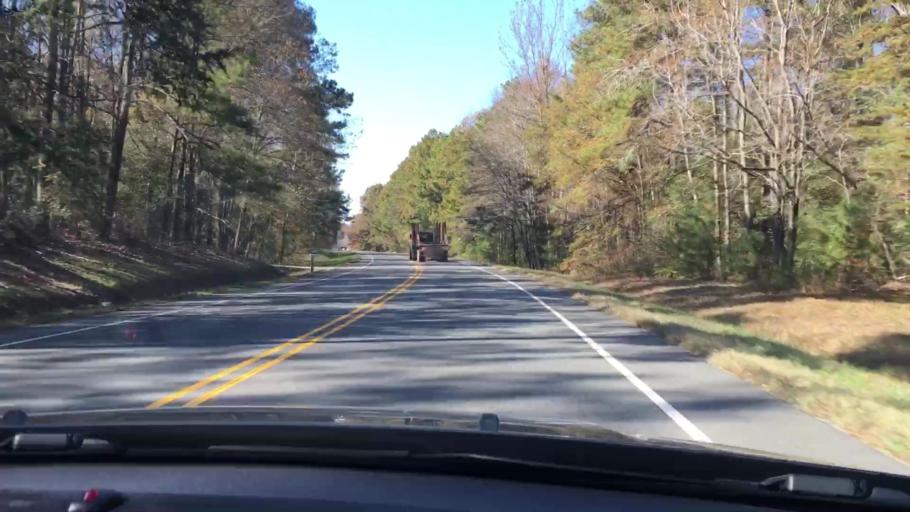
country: US
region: Virginia
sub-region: King William County
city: Central Garage
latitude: 37.7846
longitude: -77.1709
